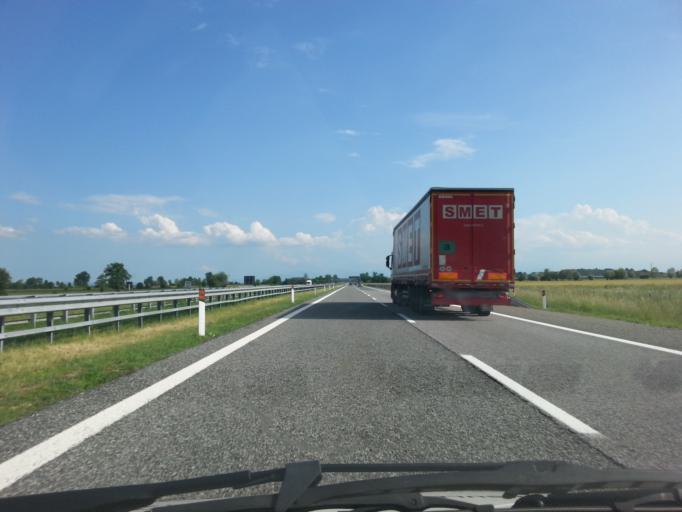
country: IT
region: Piedmont
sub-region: Provincia di Cuneo
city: Marene
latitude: 44.6867
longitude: 7.7680
